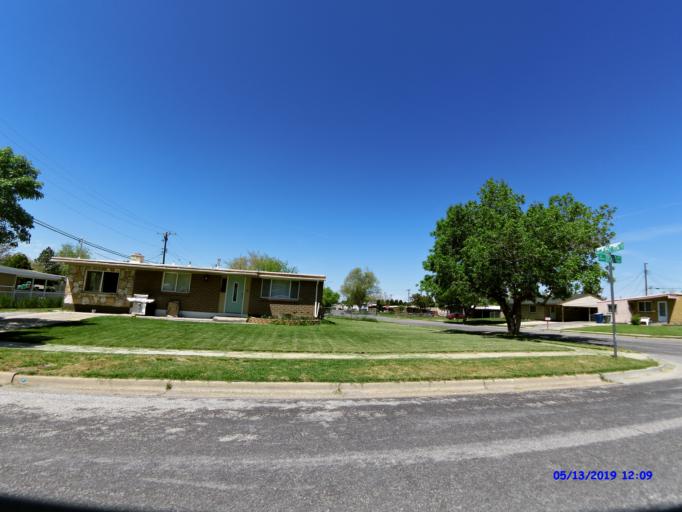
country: US
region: Utah
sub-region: Weber County
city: Harrisville
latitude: 41.2762
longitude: -111.9629
